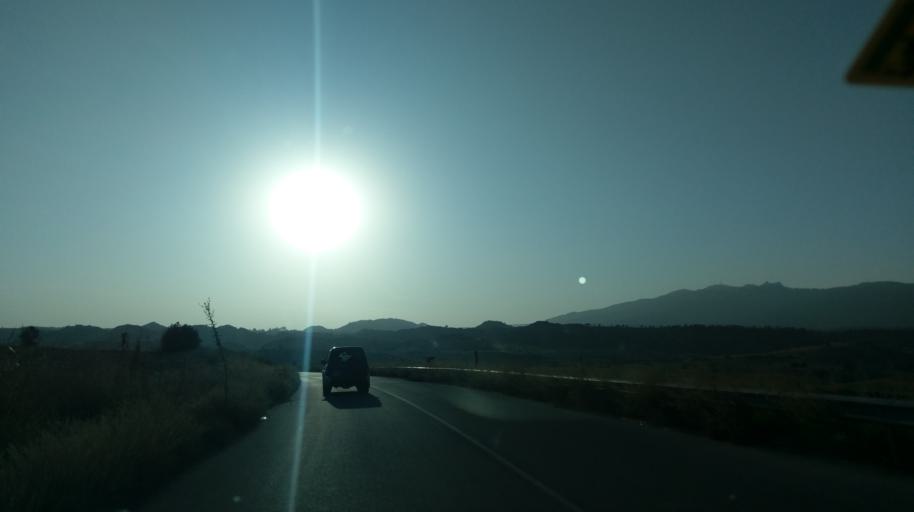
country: CY
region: Ammochostos
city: Trikomo
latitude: 35.3818
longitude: 33.9586
